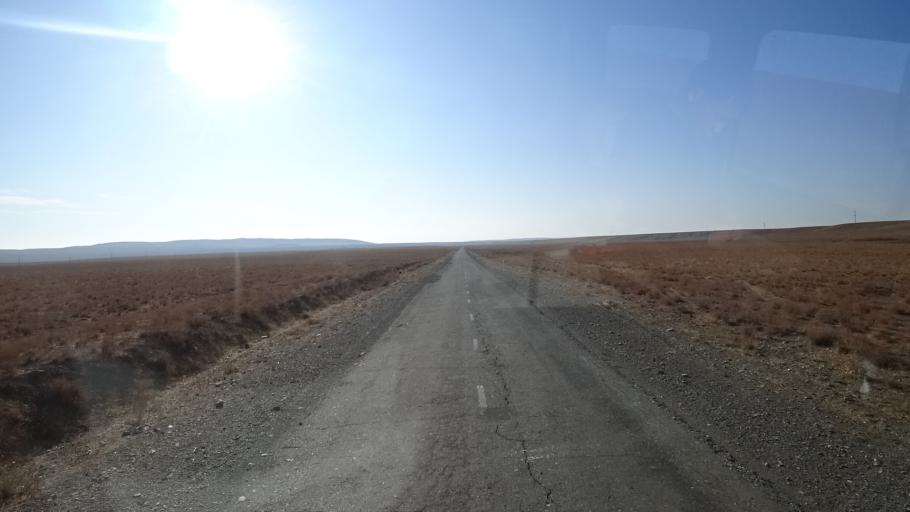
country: UZ
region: Navoiy
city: Karmana Shahri
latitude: 40.2645
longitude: 65.5071
